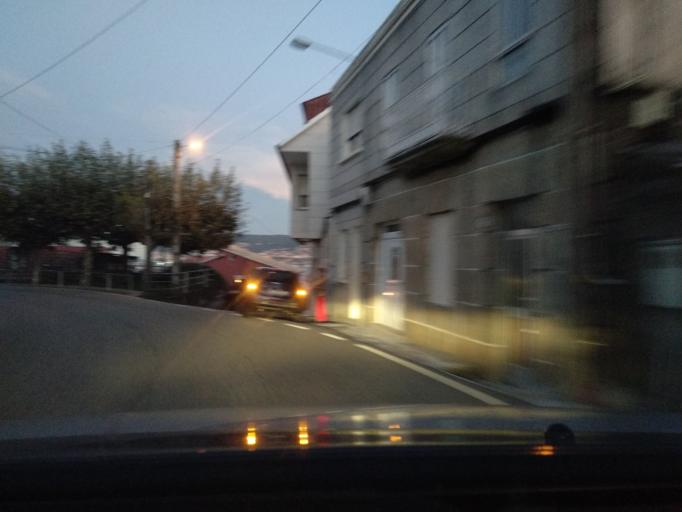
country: ES
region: Galicia
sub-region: Provincia de Pontevedra
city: Moana
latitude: 42.2810
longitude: -8.7460
